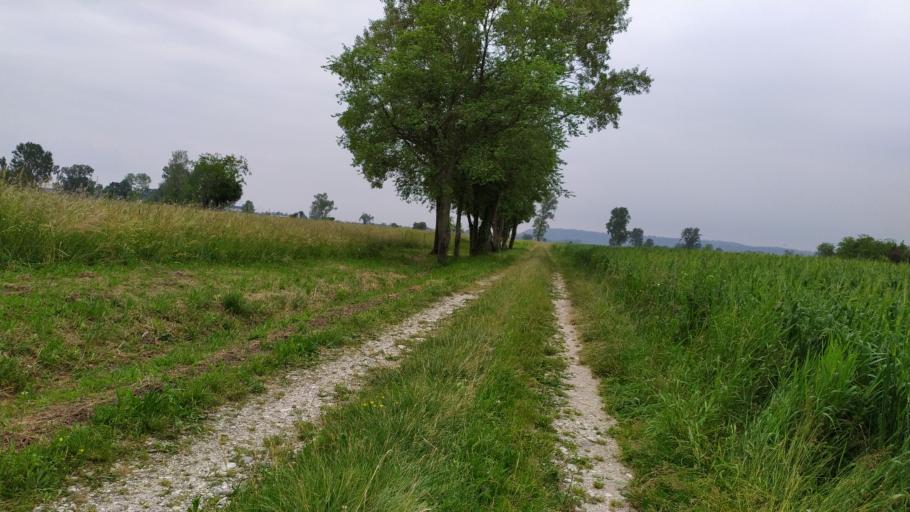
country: IT
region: Friuli Venezia Giulia
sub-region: Provincia di Udine
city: Osoppo
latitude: 46.2403
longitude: 13.0684
